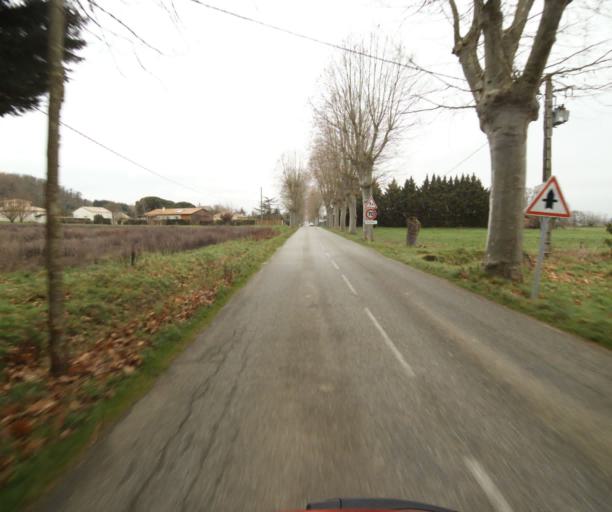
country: FR
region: Midi-Pyrenees
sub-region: Departement de la Haute-Garonne
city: Gaillac-Toulza
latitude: 43.2714
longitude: 1.5093
